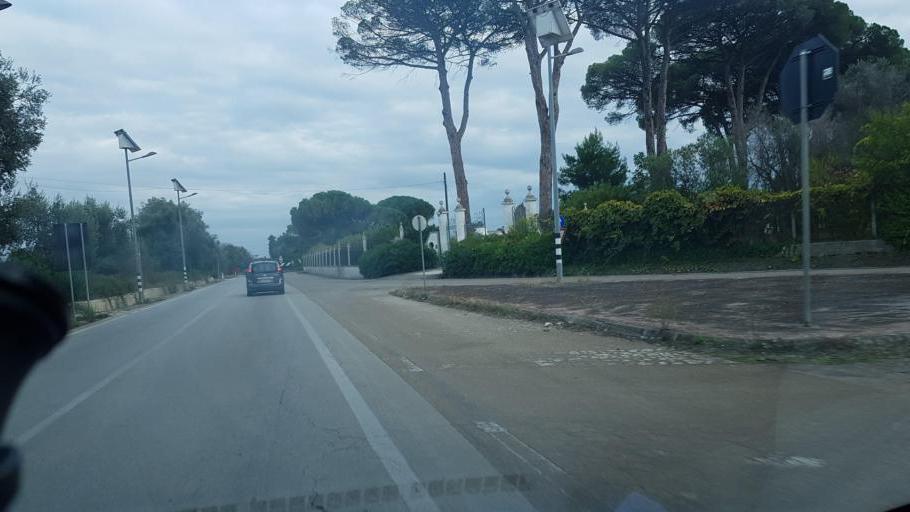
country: IT
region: Apulia
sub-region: Provincia di Brindisi
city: Francavilla Fontana
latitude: 40.5160
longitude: 17.6124
